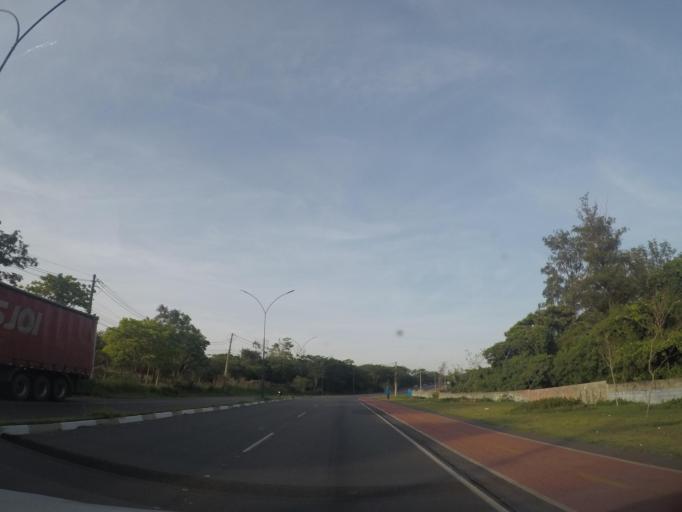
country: BR
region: Sao Paulo
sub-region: Hortolandia
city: Hortolandia
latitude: -22.8466
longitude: -47.1721
